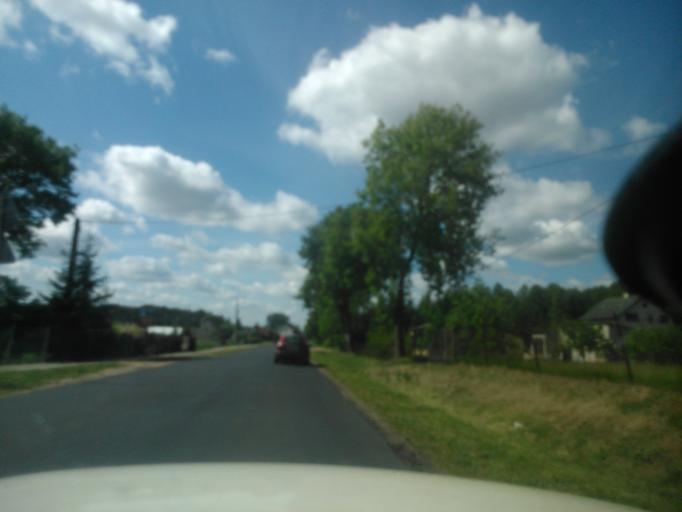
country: PL
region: Kujawsko-Pomorskie
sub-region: Powiat golubsko-dobrzynski
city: Golub-Dobrzyn
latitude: 53.1021
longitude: 19.0218
